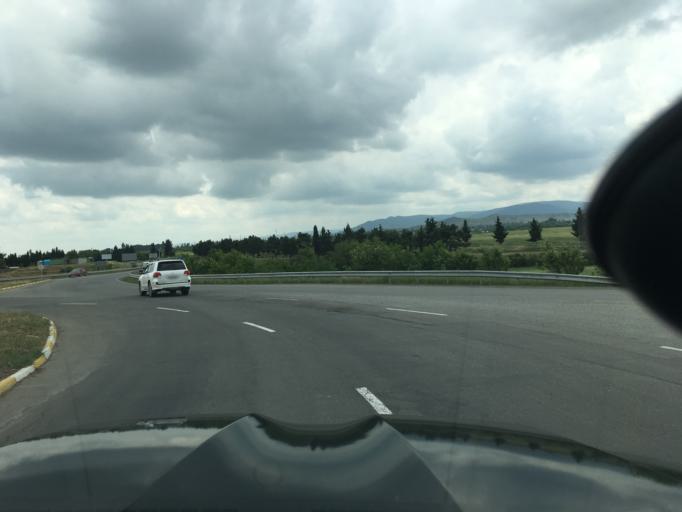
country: AZ
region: Tovuz
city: Tovuz
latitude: 40.9786
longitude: 45.6682
